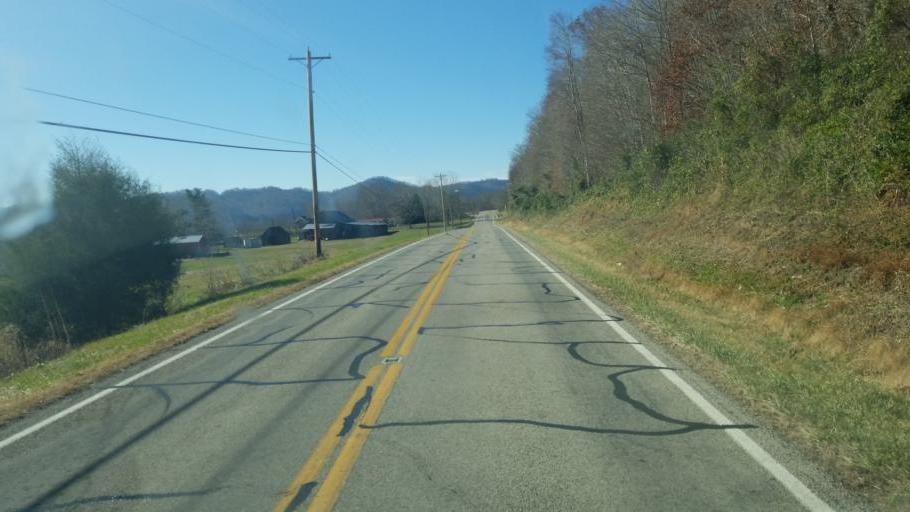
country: US
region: Kentucky
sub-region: Lewis County
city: Vanceburg
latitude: 38.6240
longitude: -83.1699
